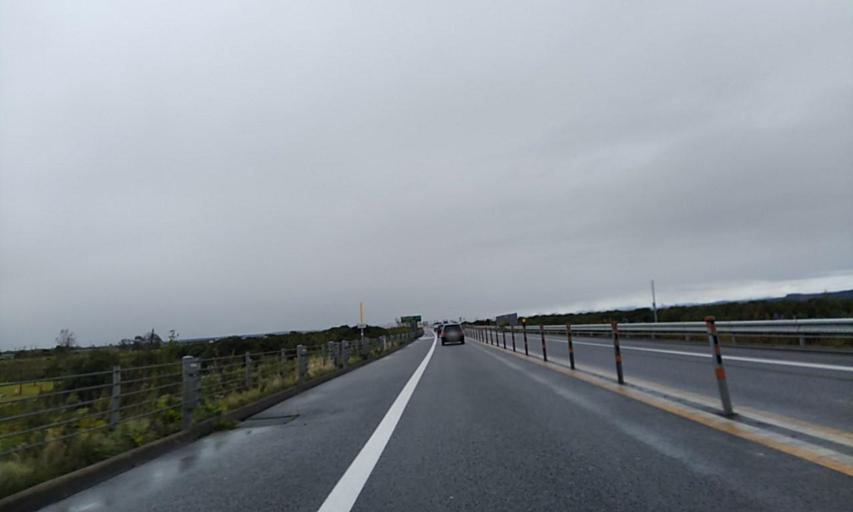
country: JP
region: Hokkaido
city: Kushiro
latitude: 43.0364
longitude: 144.3585
